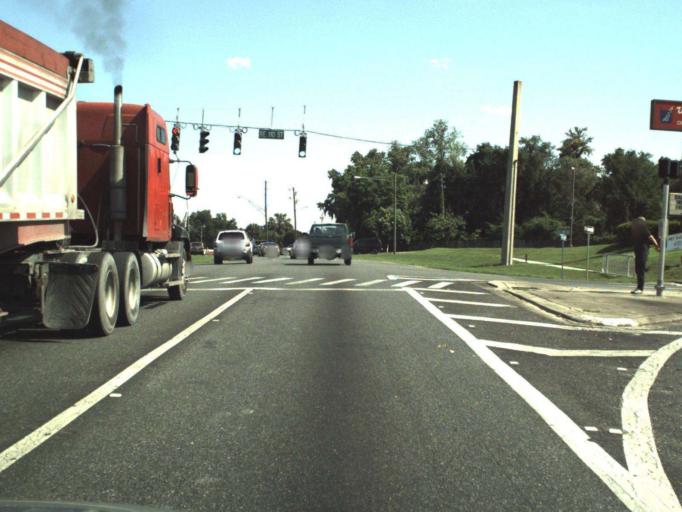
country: US
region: Florida
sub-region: Marion County
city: Belleview
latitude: 29.0628
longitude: -82.0667
